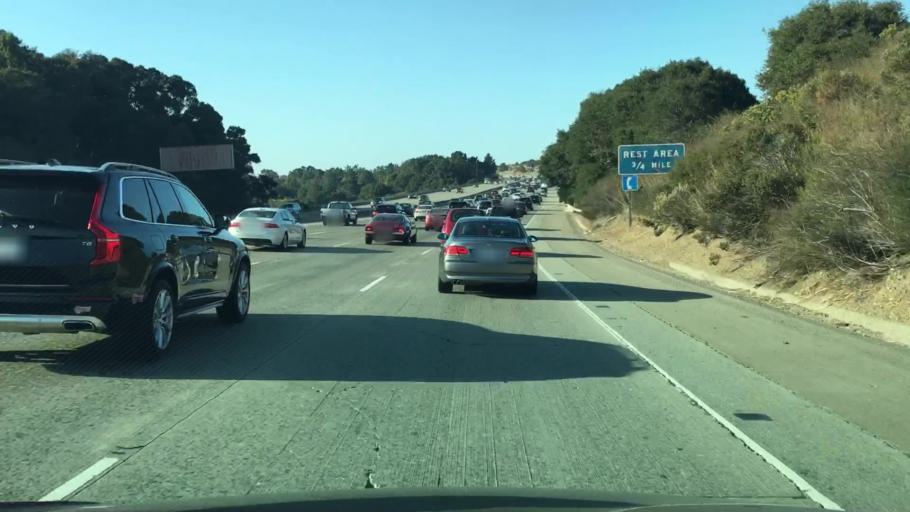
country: US
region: California
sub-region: San Mateo County
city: Highlands-Baywood Park
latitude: 37.5273
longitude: -122.3591
